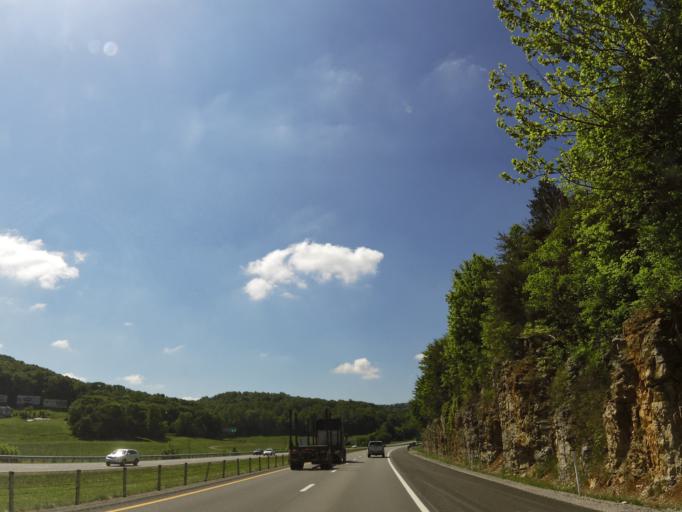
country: US
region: Kentucky
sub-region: Rockcastle County
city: Mount Vernon
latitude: 37.3615
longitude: -84.3090
